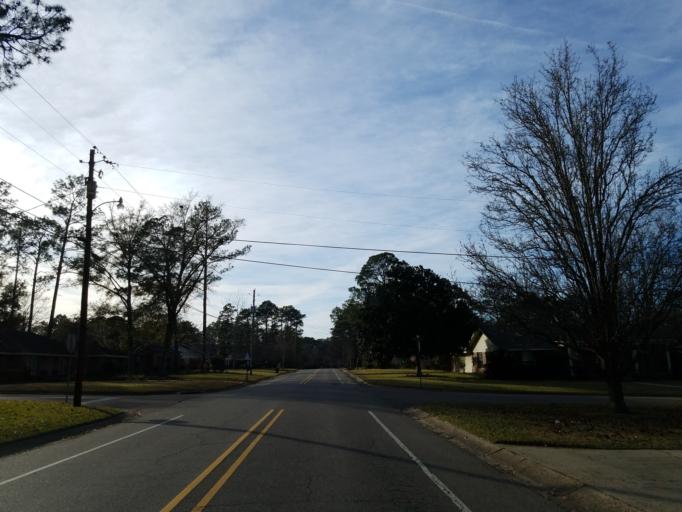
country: US
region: Mississippi
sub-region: Lamar County
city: West Hattiesburg
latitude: 31.3115
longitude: -89.3419
